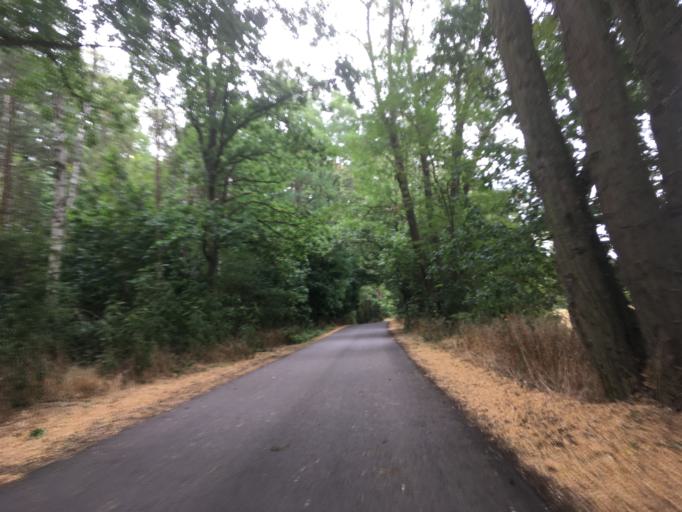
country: DE
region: Brandenburg
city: Chorin
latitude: 52.9034
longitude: 13.8568
